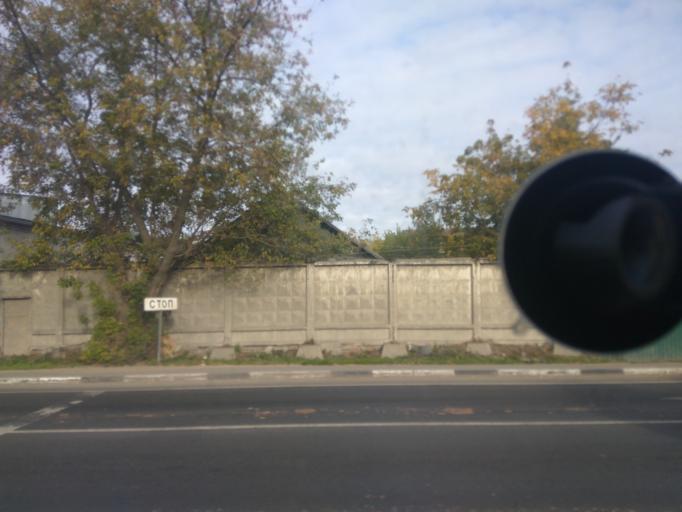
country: RU
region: Moscow
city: Vostochnyy
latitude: 55.8199
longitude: 37.8581
